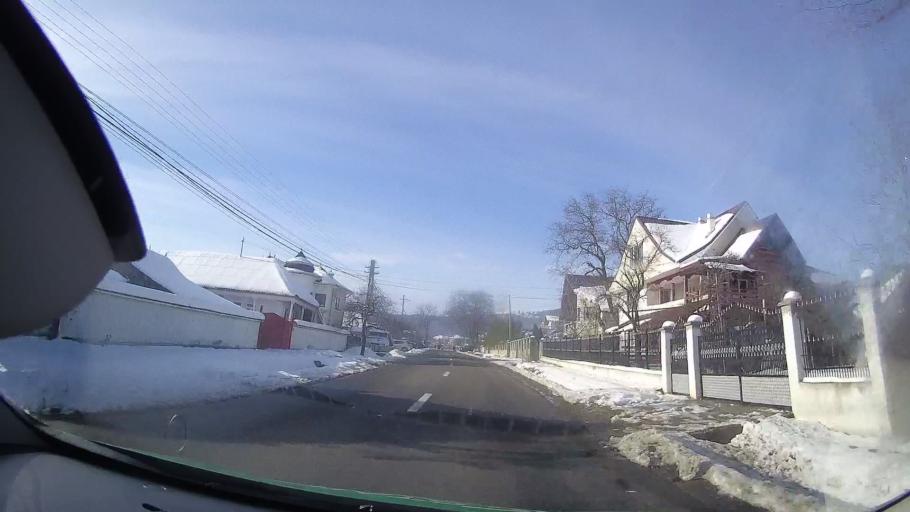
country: RO
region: Neamt
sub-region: Comuna Agapia
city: Agapia
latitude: 47.1728
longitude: 26.2894
